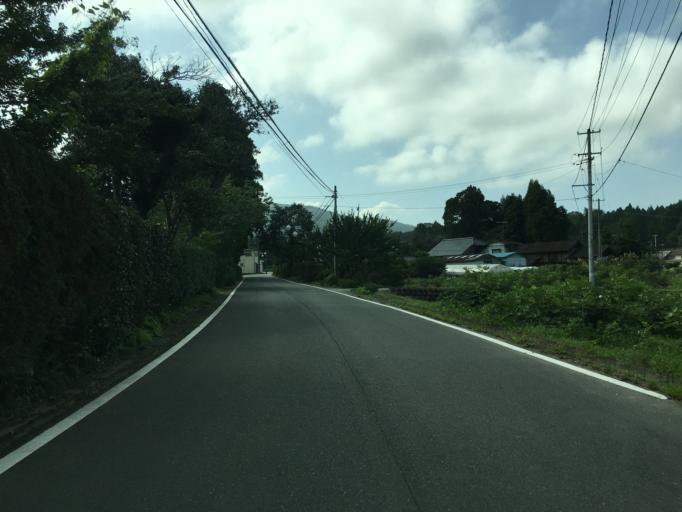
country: JP
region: Miyagi
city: Marumori
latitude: 37.8905
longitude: 140.8847
